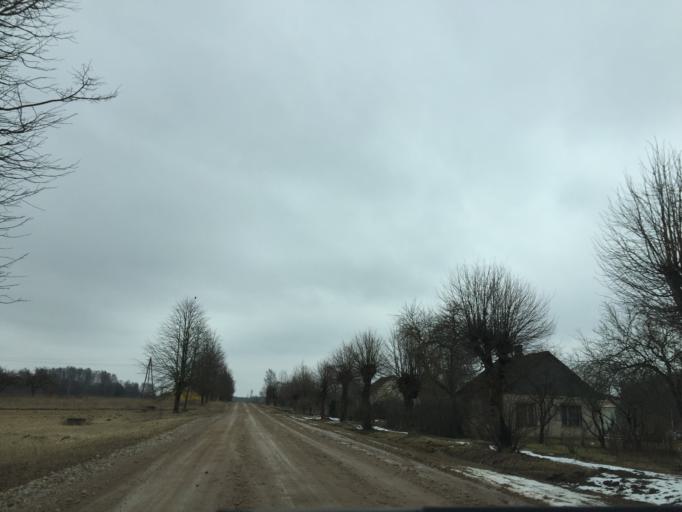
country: LV
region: Lielvarde
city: Lielvarde
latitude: 56.7573
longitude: 24.7875
